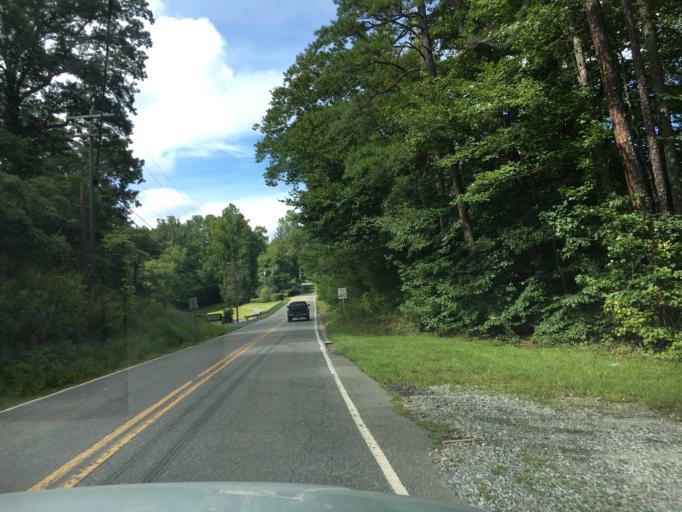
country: US
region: North Carolina
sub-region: Polk County
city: Columbus
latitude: 35.2705
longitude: -82.1828
